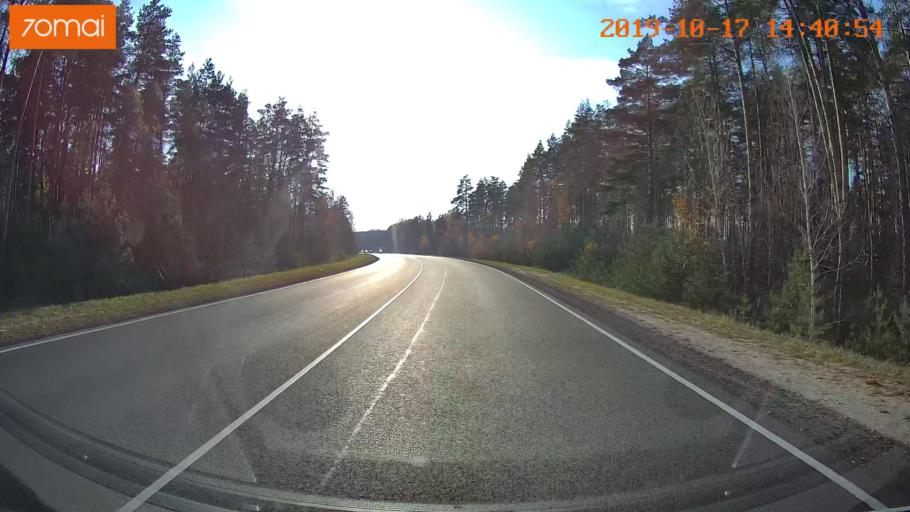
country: RU
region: Rjazan
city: Solotcha
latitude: 54.8515
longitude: 39.9472
